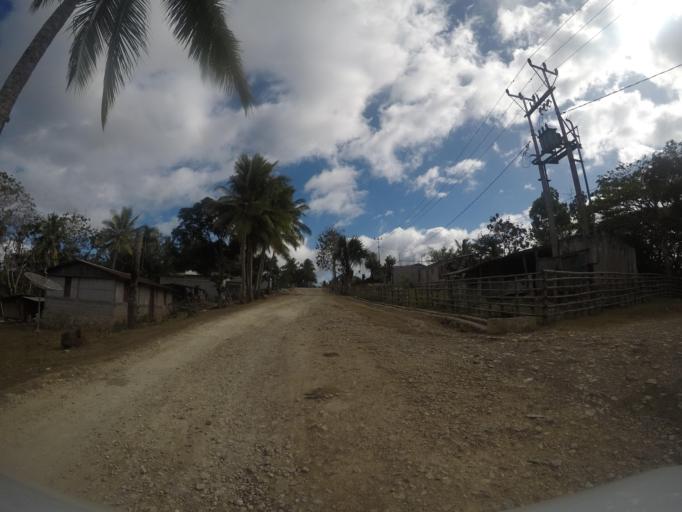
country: TL
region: Lautem
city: Lospalos
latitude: -8.5681
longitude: 126.8847
